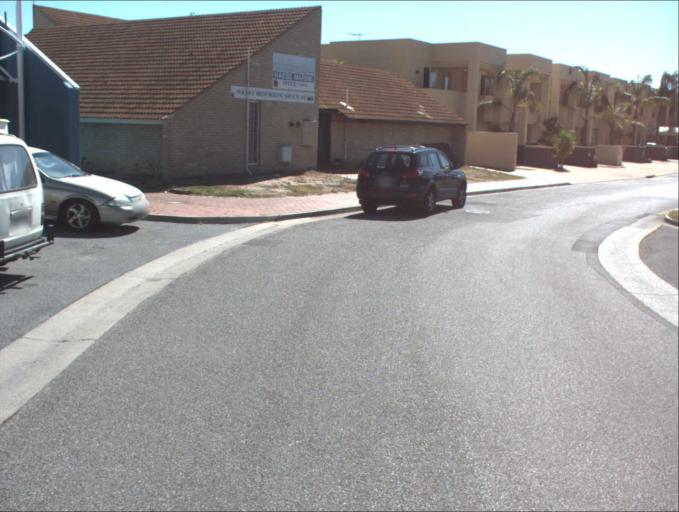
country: AU
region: South Australia
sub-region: Port Adelaide Enfield
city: Birkenhead
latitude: -34.7858
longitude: 138.4892
